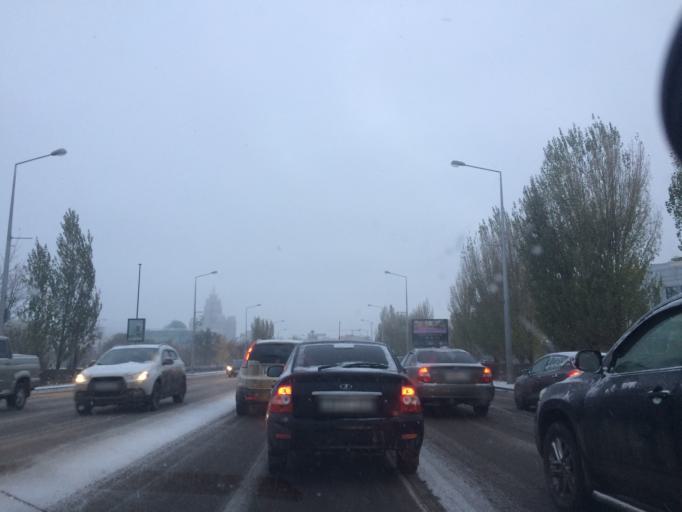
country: KZ
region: Astana Qalasy
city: Astana
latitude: 51.1503
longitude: 71.4124
